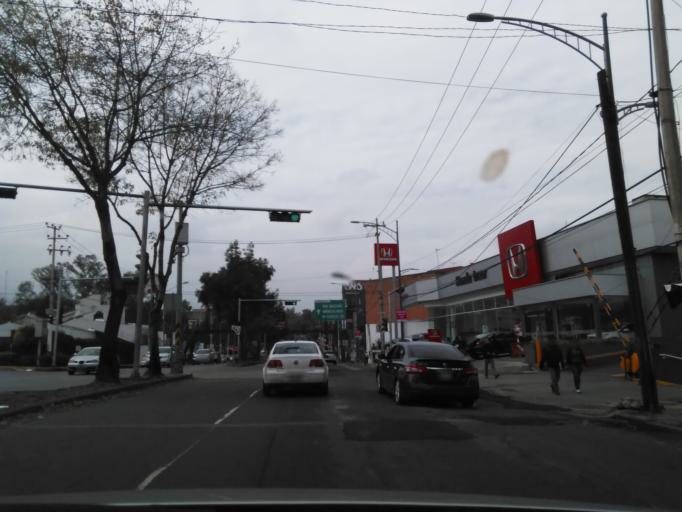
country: MX
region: Mexico City
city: Tlalpan
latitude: 19.2798
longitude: -99.1686
